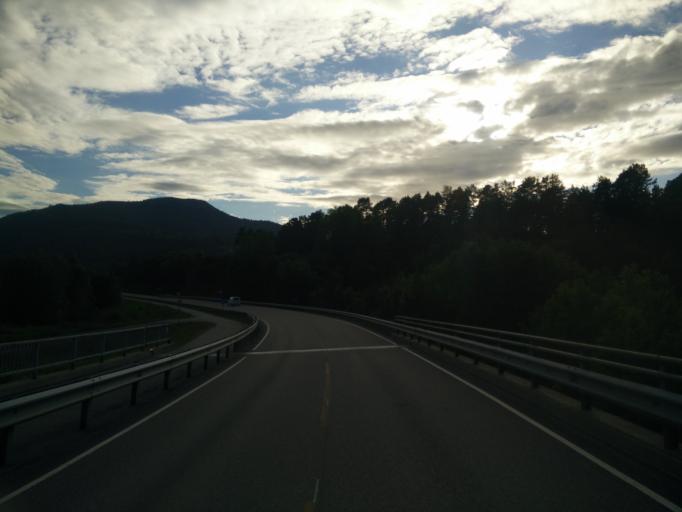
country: NO
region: More og Romsdal
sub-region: Kristiansund
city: Rensvik
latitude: 63.0128
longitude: 7.9842
